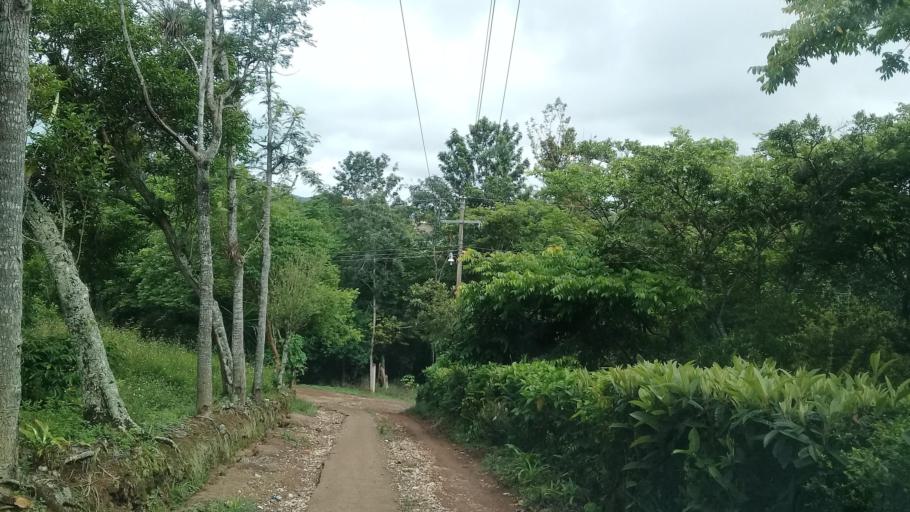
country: MX
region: Veracruz
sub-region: Emiliano Zapata
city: Jacarandas
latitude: 19.4782
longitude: -96.8506
